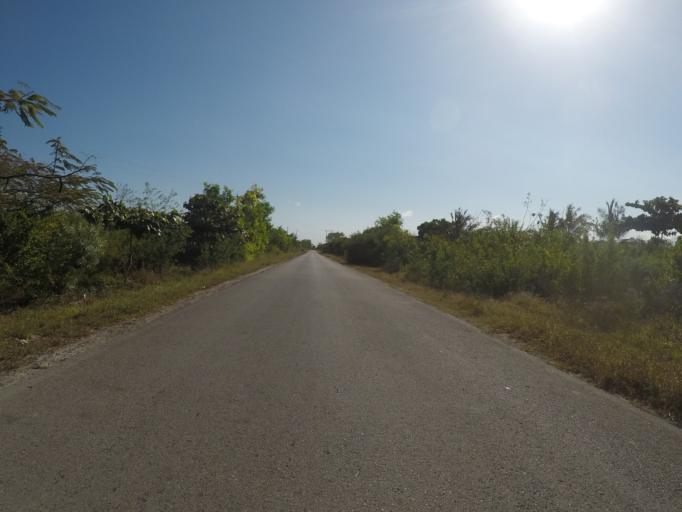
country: TZ
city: Kiwengwa
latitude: -6.1429
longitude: 39.5082
